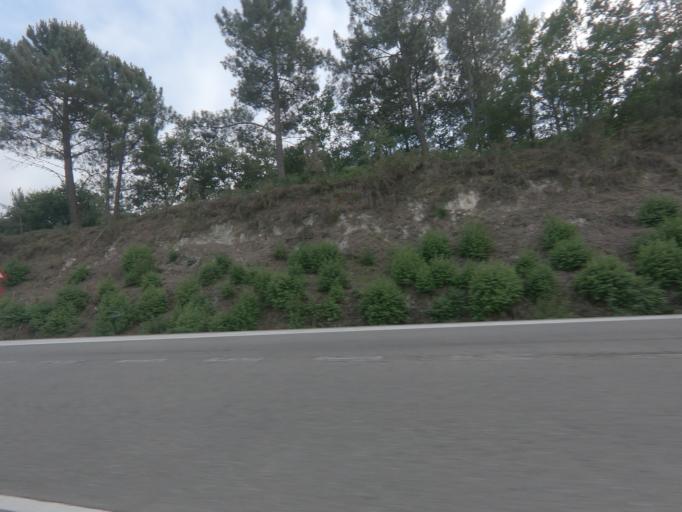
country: ES
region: Galicia
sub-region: Provincia de Ourense
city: Taboadela
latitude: 42.2153
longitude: -7.8319
